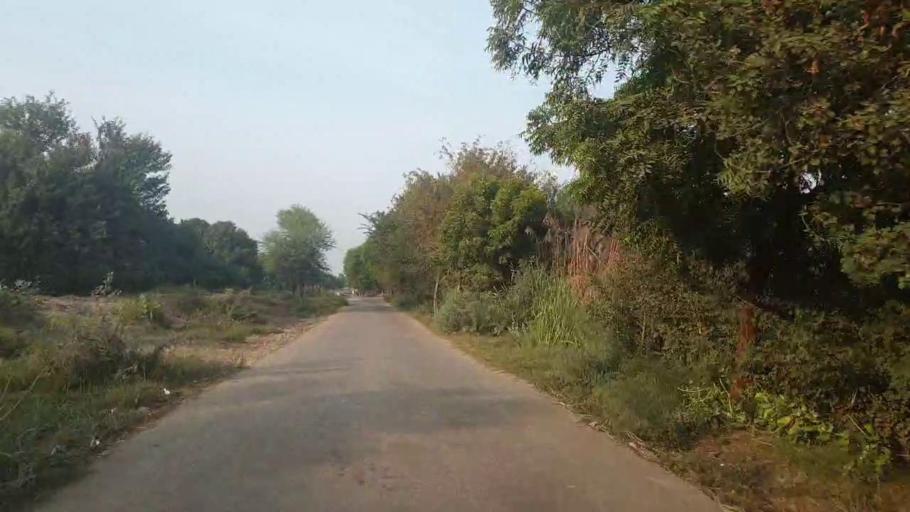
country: PK
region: Sindh
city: Tando Jam
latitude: 25.4473
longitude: 68.5849
